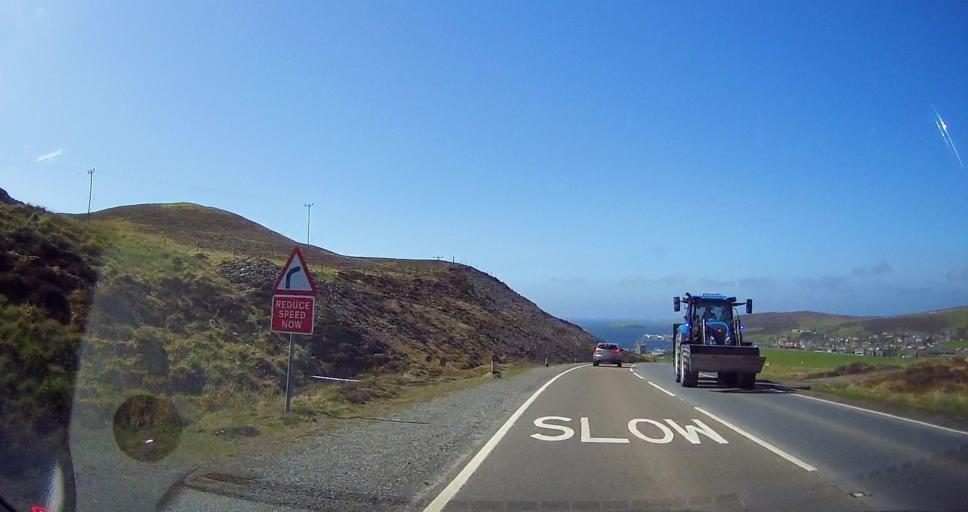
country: GB
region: Scotland
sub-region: Shetland Islands
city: Lerwick
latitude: 60.1398
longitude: -1.2572
